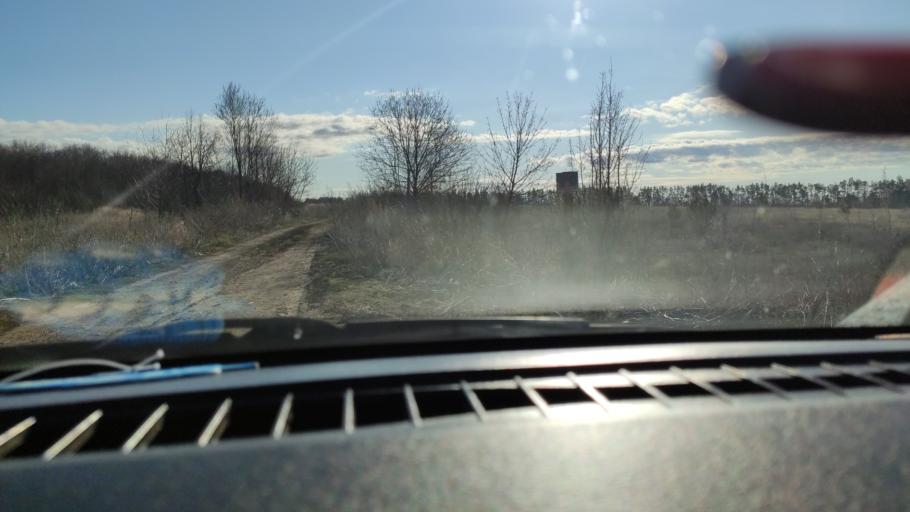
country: RU
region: Saratov
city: Dukhovnitskoye
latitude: 52.7092
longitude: 48.2643
